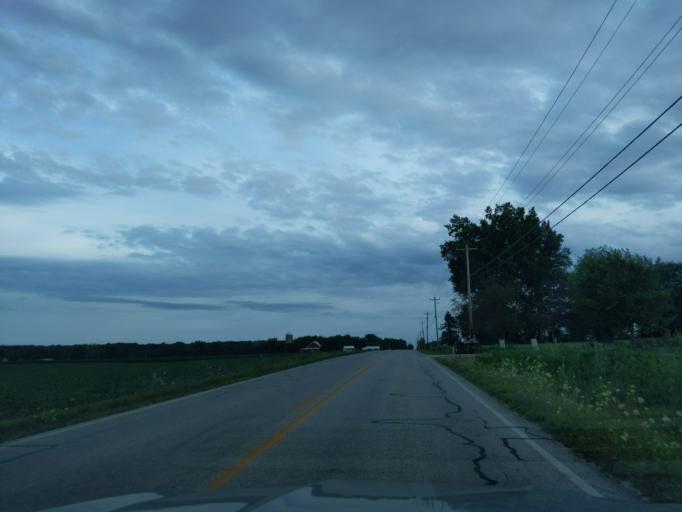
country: US
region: Indiana
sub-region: Ripley County
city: Sunman
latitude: 39.2563
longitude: -85.0945
